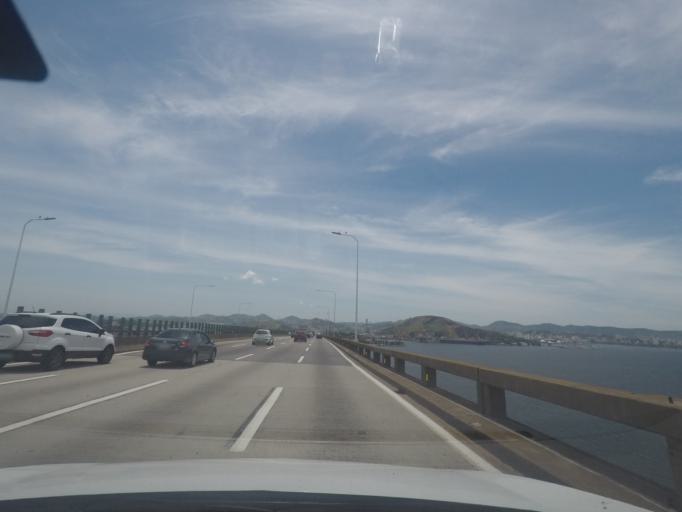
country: BR
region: Rio de Janeiro
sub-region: Niteroi
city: Niteroi
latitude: -22.8717
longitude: -43.1510
